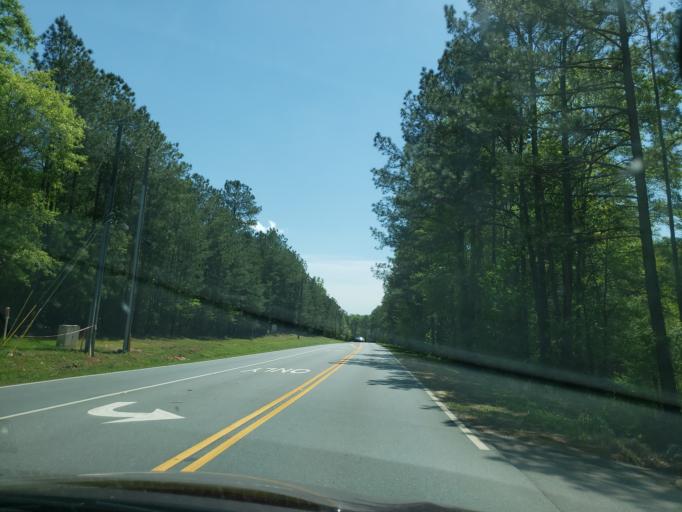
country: US
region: Alabama
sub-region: Lee County
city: Auburn
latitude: 32.6488
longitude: -85.5137
